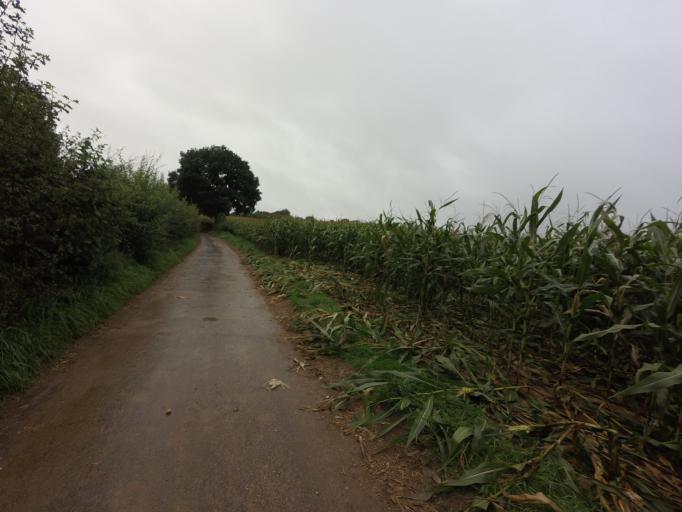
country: NL
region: Limburg
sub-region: Eijsden-Margraten
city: Margraten
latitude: 50.8154
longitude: 5.7741
